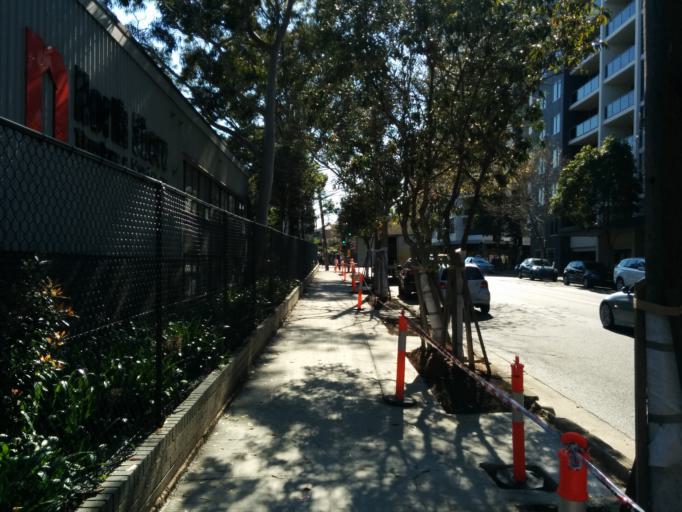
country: AU
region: New South Wales
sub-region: City of Sydney
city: Redfern
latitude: -33.8985
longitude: 151.2120
